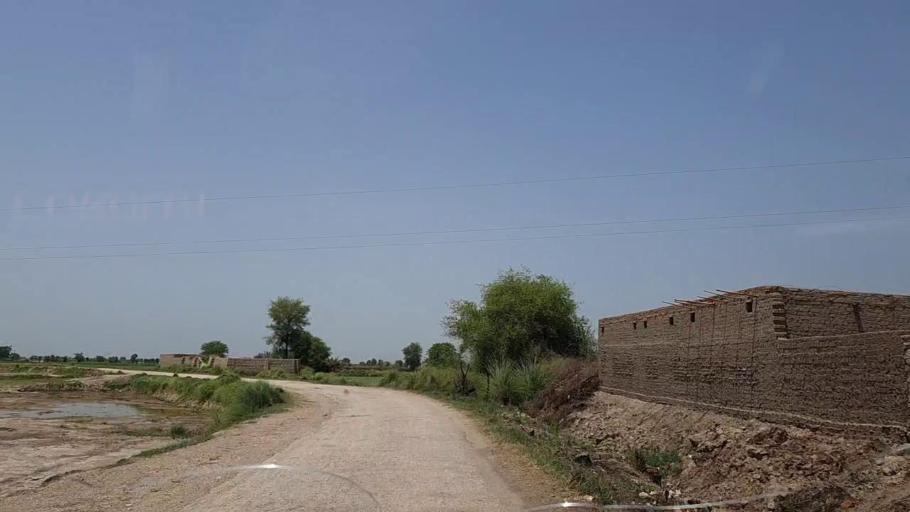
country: PK
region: Sindh
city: Tharu Shah
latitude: 26.9256
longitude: 68.0558
